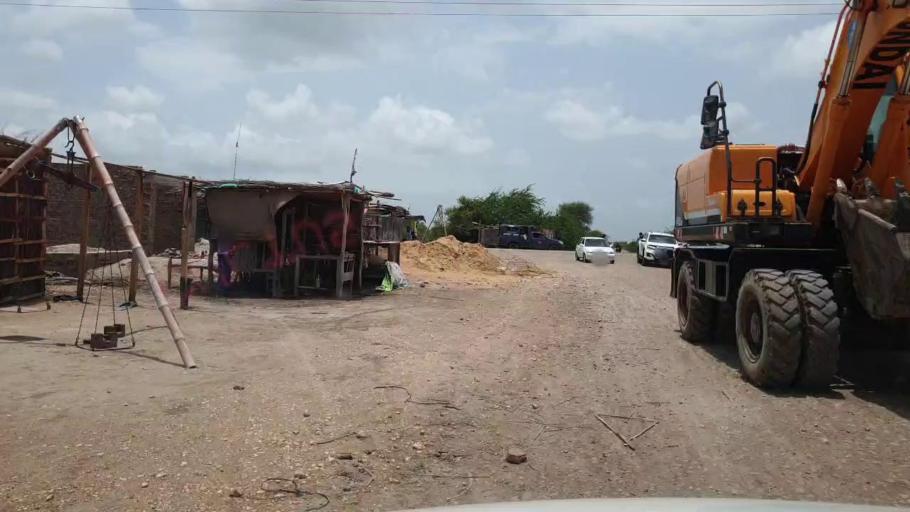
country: PK
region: Sindh
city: Kario
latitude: 24.7244
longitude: 68.5621
